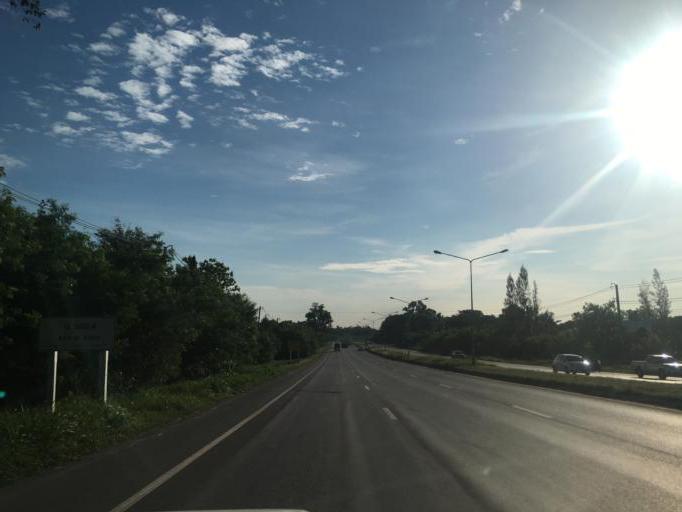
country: TH
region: Changwat Udon Thani
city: Kut Chap
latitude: 17.3329
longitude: 102.6575
